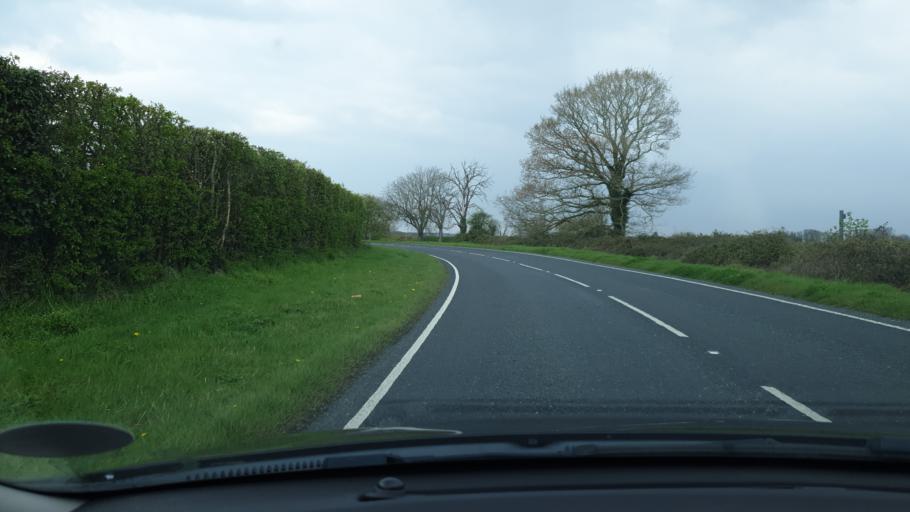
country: GB
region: England
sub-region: Essex
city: Mistley
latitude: 51.9274
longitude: 1.0833
